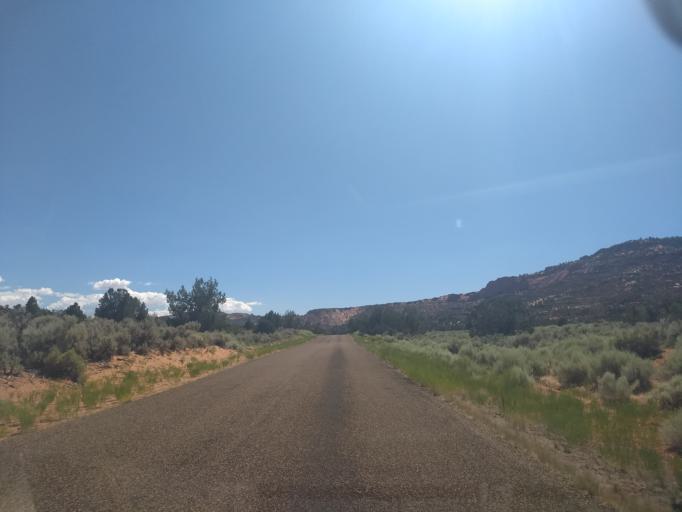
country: US
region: Utah
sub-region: Washington County
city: Hildale
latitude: 37.0077
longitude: -112.8527
